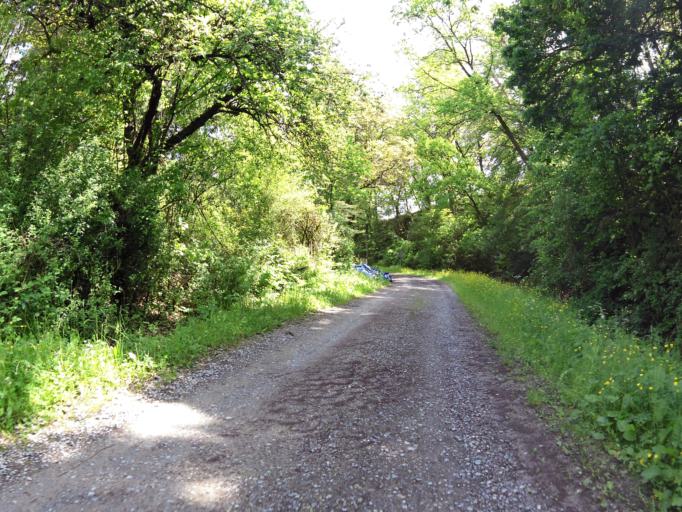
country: DE
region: Bavaria
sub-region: Regierungsbezirk Unterfranken
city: Winterhausen
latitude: 49.7218
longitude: 10.0164
